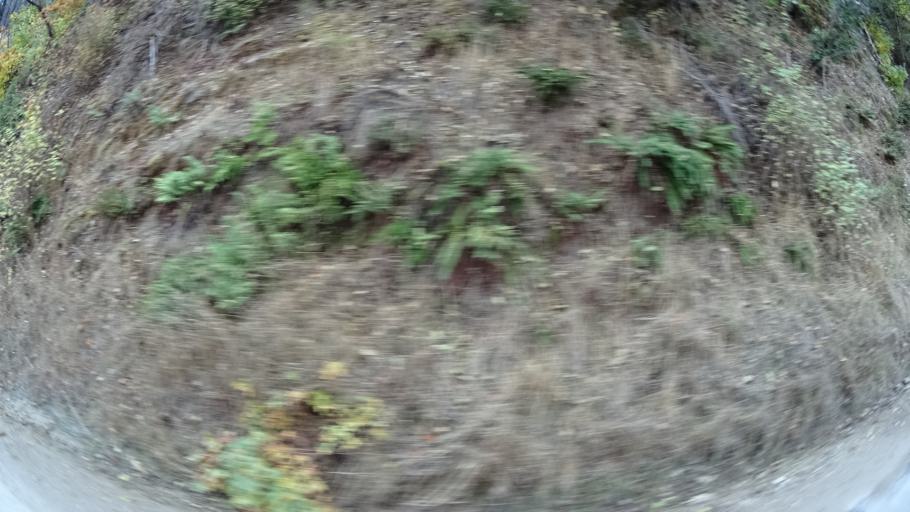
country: US
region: California
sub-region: Siskiyou County
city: Happy Camp
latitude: 41.7689
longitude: -123.3415
